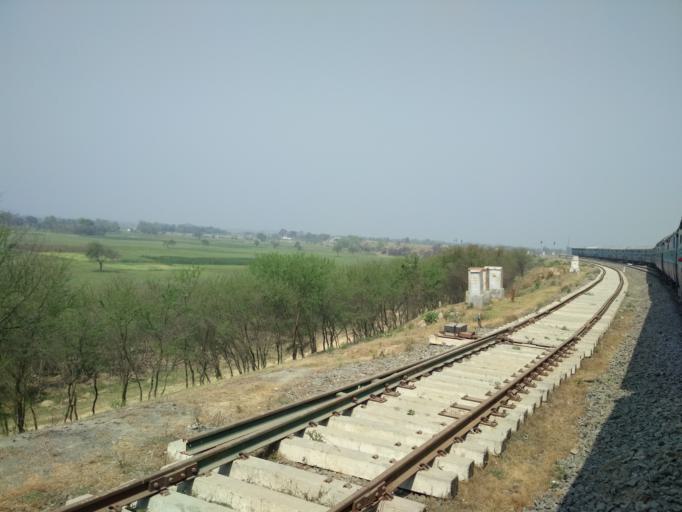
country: IN
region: Bihar
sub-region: Munger
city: Munger
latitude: 25.4317
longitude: 86.4389
